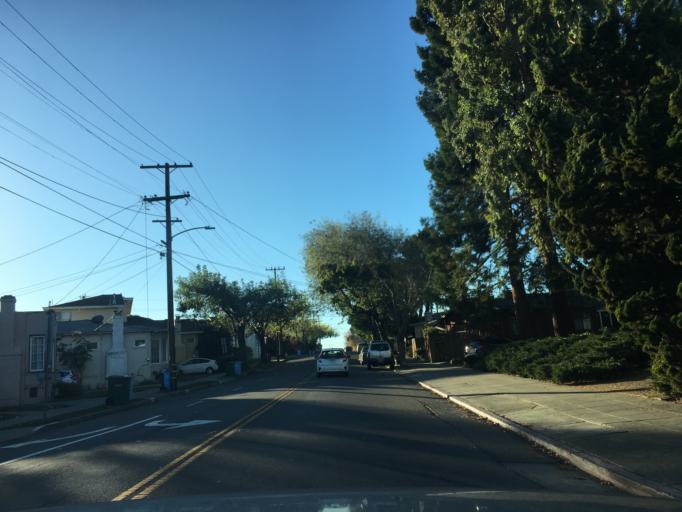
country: US
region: California
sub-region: Alameda County
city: Berkeley
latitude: 37.8809
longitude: -122.2832
